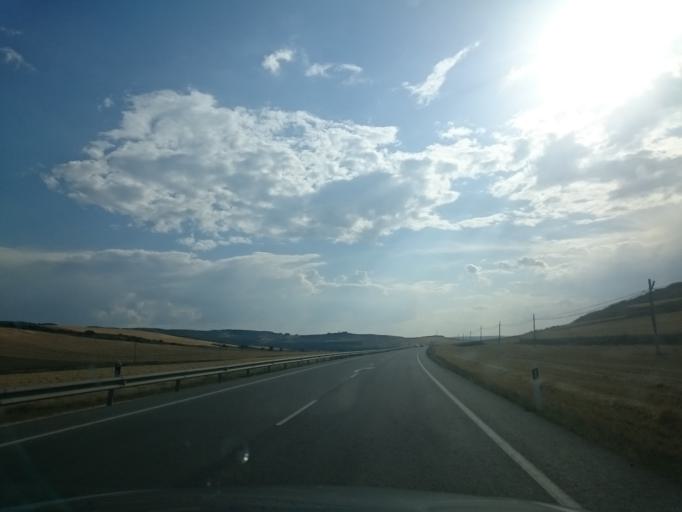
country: ES
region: Castille and Leon
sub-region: Provincia de Burgos
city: Fresnena
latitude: 42.4208
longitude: -3.1583
